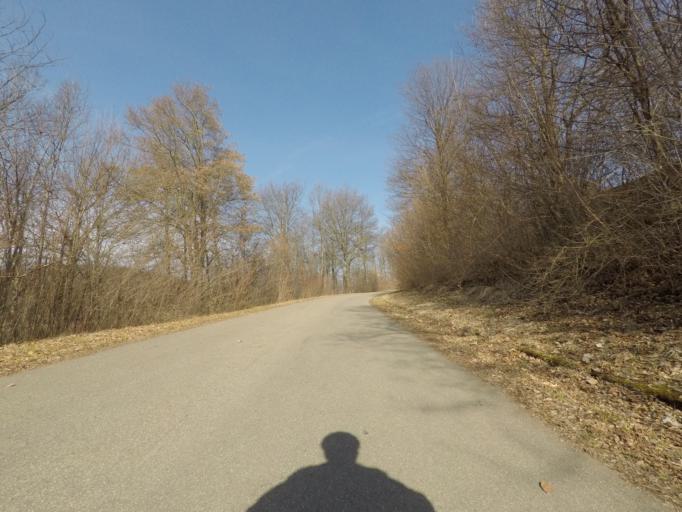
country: DE
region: Baden-Wuerttemberg
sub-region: Tuebingen Region
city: Metzingen
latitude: 48.5058
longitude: 9.2878
